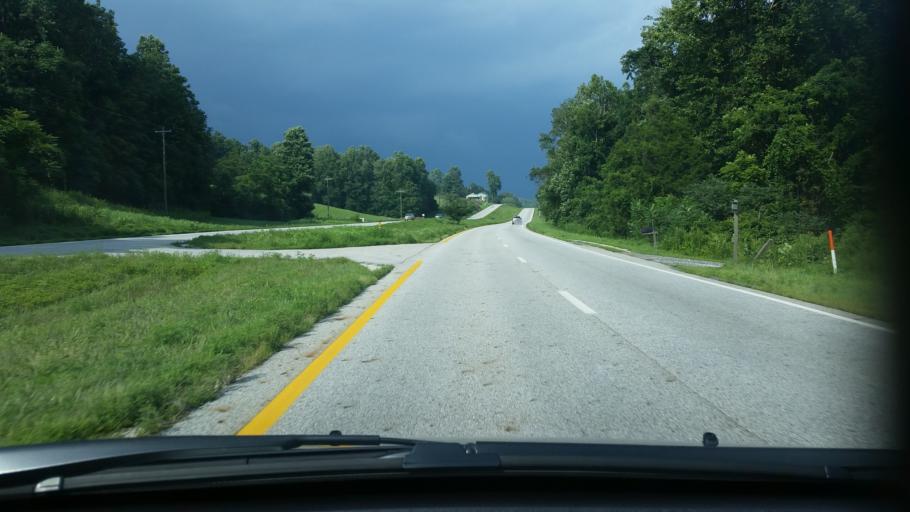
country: US
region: Virginia
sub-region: Nelson County
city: Lovingston
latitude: 37.8087
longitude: -78.8586
